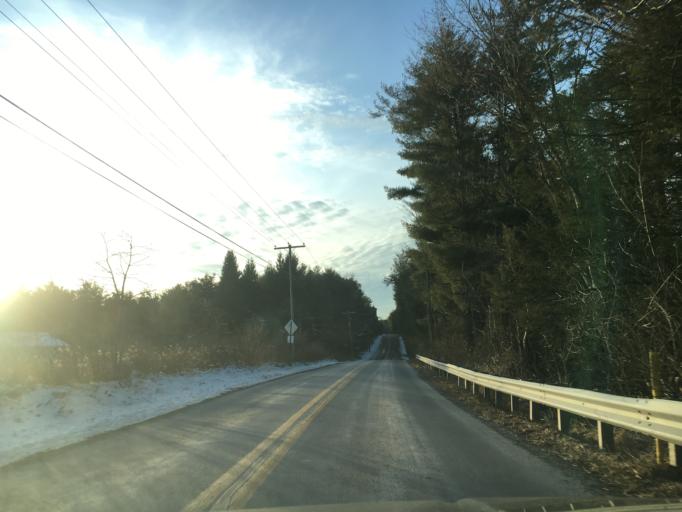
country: US
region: Pennsylvania
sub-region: Pike County
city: Hemlock Farms
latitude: 41.3727
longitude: -75.1201
